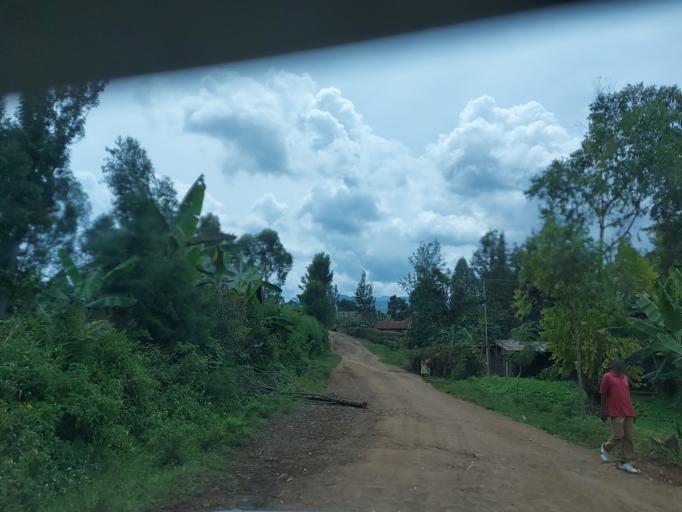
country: CD
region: South Kivu
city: Bukavu
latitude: -2.2441
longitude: 28.8186
